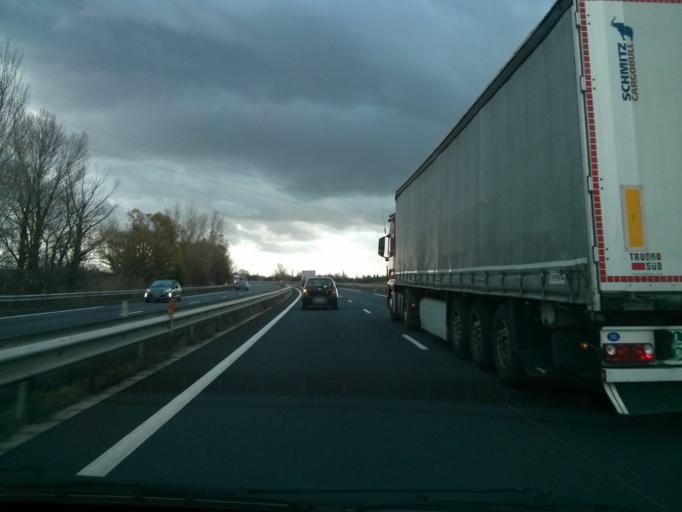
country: FR
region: Languedoc-Roussillon
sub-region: Departement du Gard
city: Bellegarde
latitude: 43.7155
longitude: 4.5119
